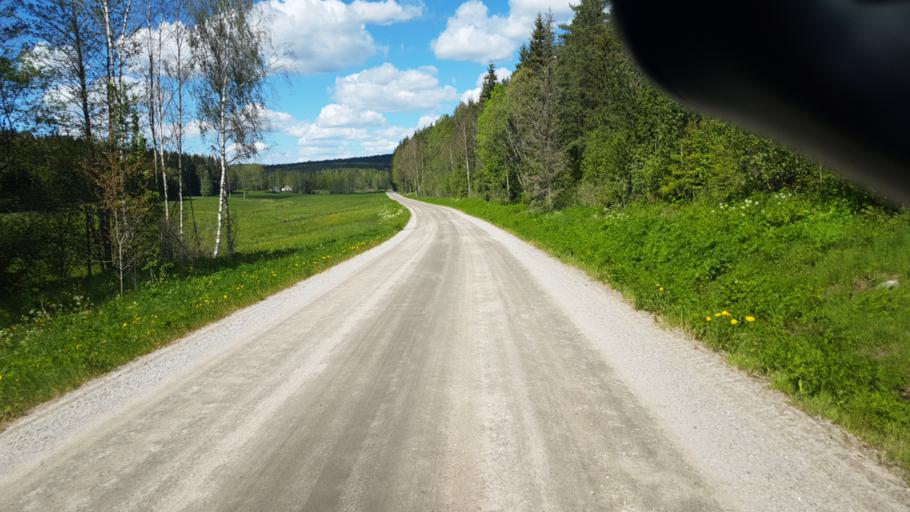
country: SE
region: Vaermland
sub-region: Arvika Kommun
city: Arvika
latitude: 59.6129
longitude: 12.9040
